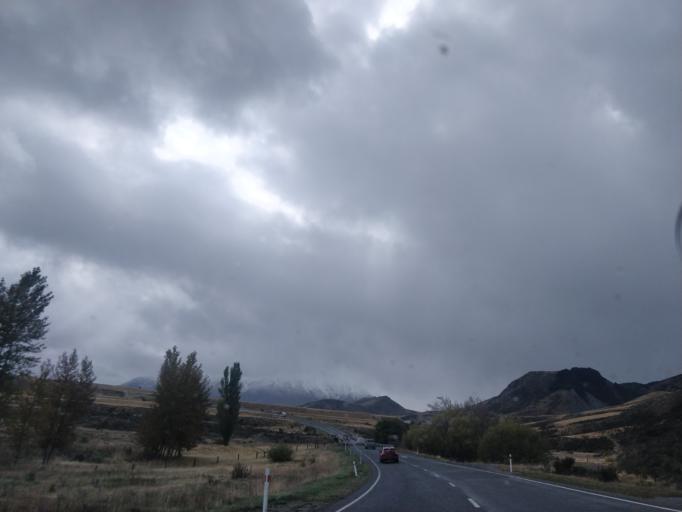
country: NZ
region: Canterbury
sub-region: Ashburton District
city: Methven
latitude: -43.2464
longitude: 171.7243
